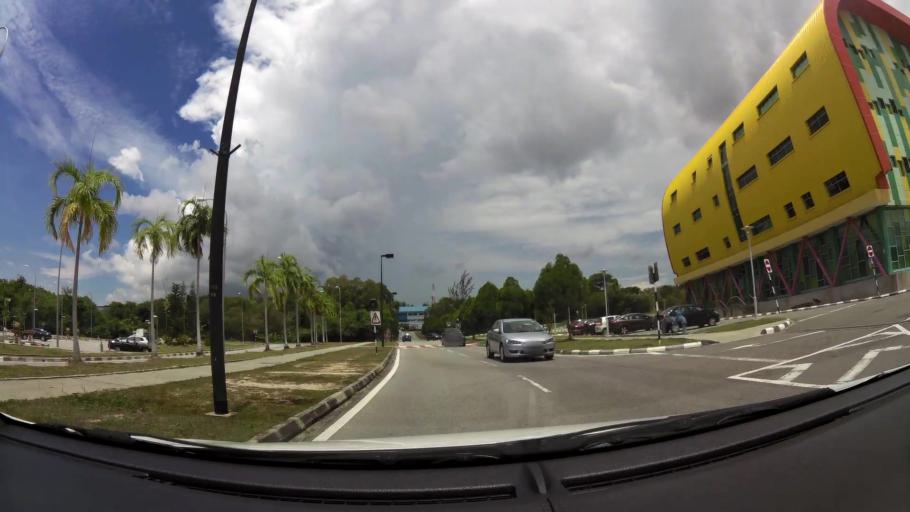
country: BN
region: Brunei and Muara
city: Bandar Seri Begawan
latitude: 4.9789
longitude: 114.8976
